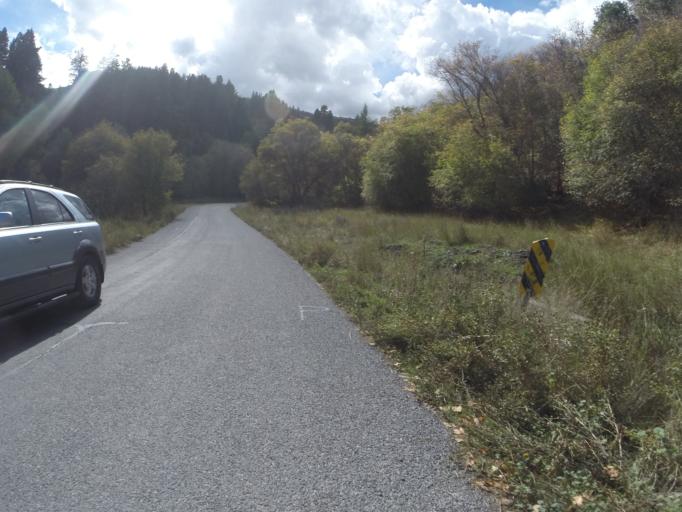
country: US
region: Utah
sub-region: Salt Lake County
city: Herriman
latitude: 40.4853
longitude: -112.1438
